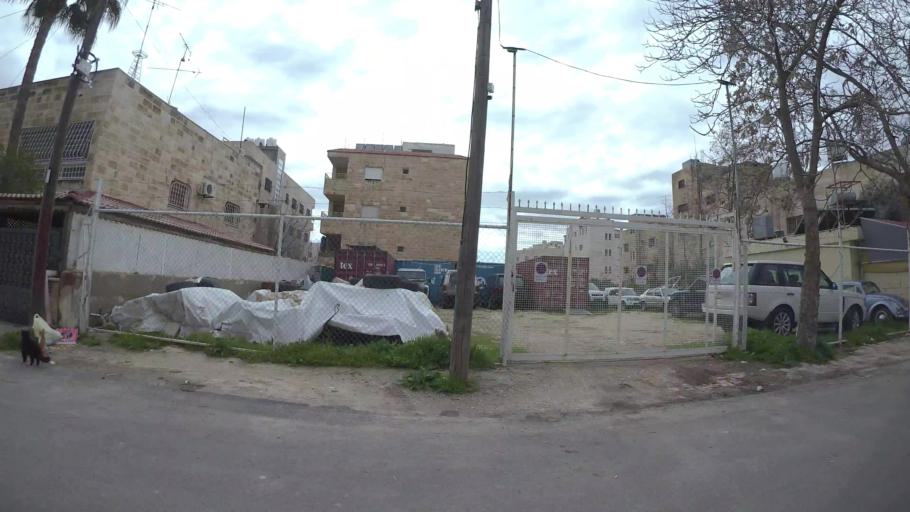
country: JO
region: Amman
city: Wadi as Sir
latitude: 31.9479
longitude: 35.8386
